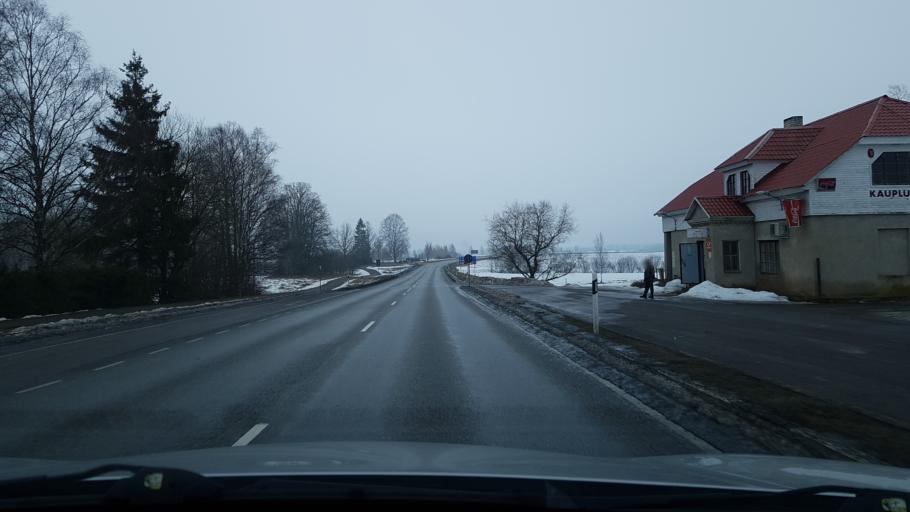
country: EE
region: Valgamaa
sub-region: Valga linn
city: Valga
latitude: 57.9231
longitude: 26.1793
